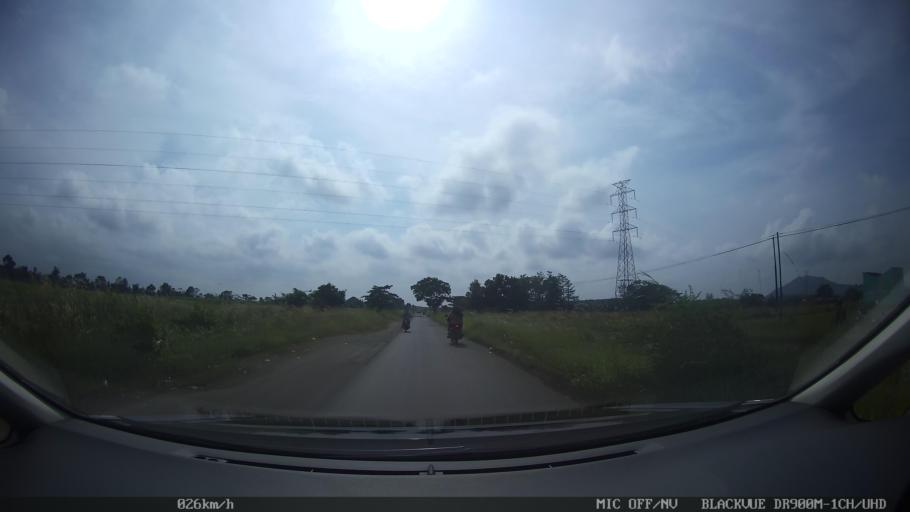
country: ID
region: Lampung
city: Kedaton
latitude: -5.3734
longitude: 105.3115
